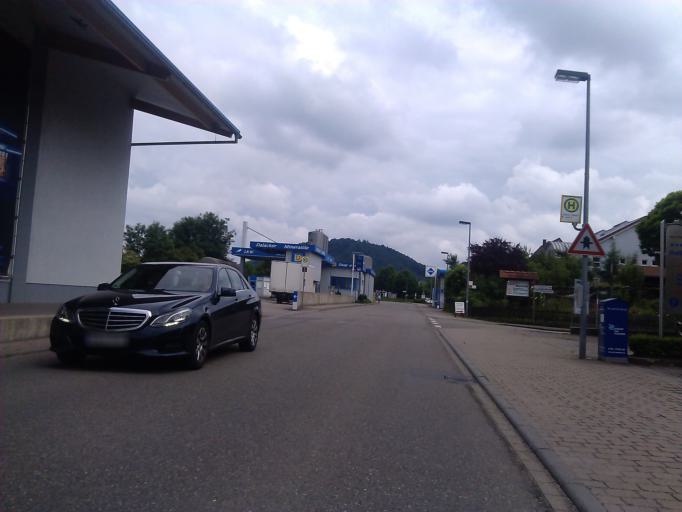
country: DE
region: Baden-Wuerttemberg
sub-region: Regierungsbezirk Stuttgart
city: Gaildorf
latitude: 48.9800
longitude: 9.7784
